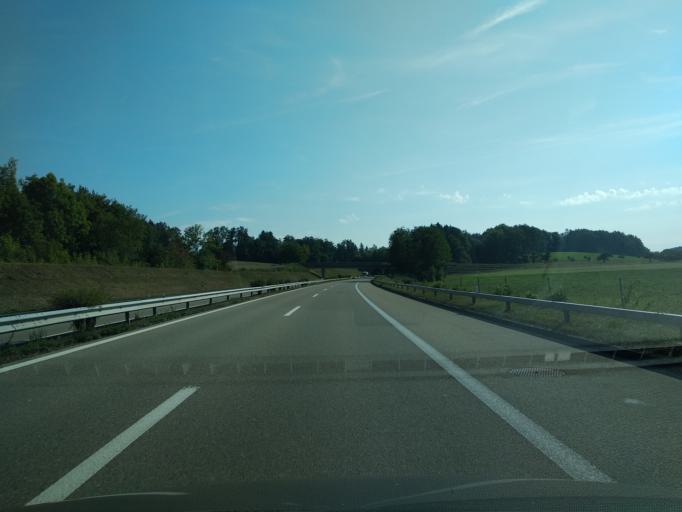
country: CH
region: Thurgau
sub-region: Weinfelden District
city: Wigoltingen
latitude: 47.6029
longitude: 9.0193
